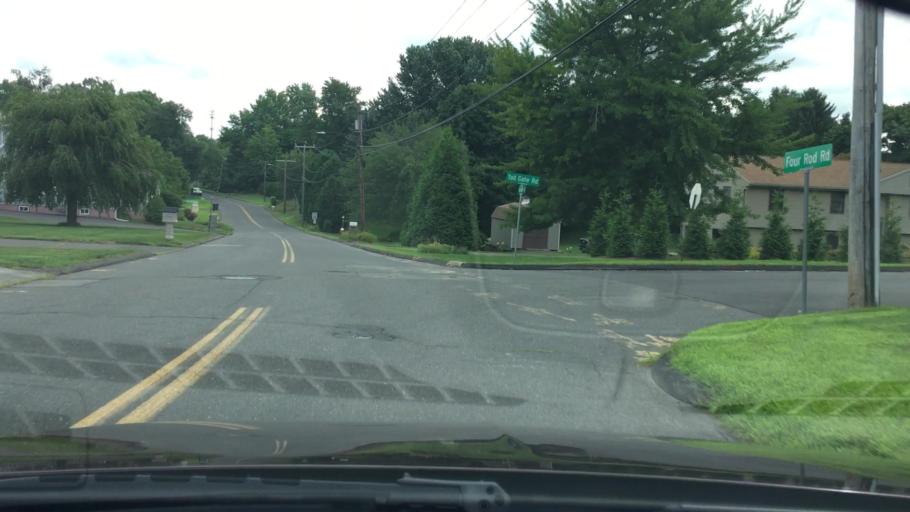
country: US
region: Connecticut
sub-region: Hartford County
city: Kensington
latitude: 41.6042
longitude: -72.7609
